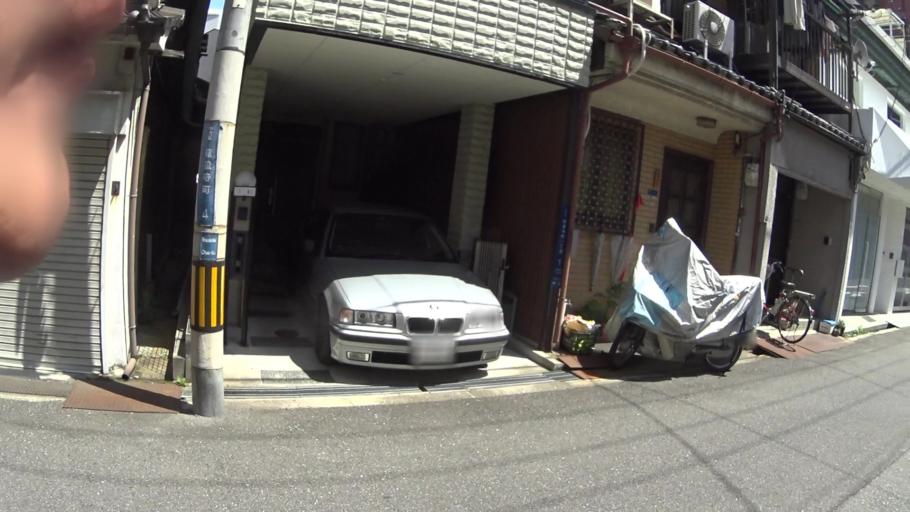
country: JP
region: Osaka
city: Osaka-shi
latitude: 34.6781
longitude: 135.5195
